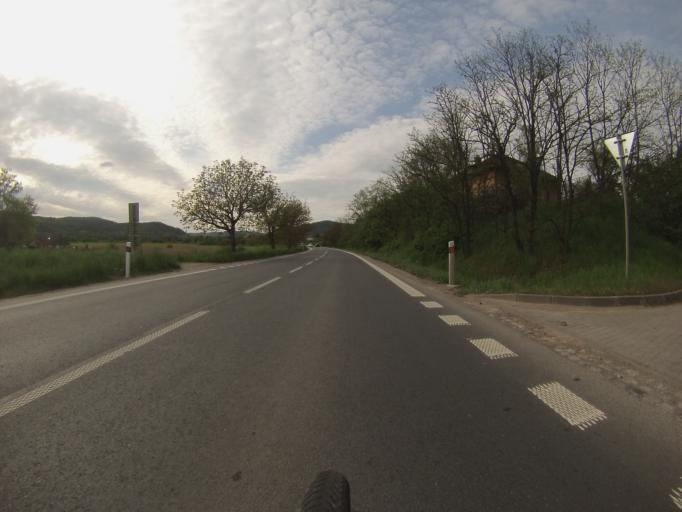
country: CZ
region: South Moravian
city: Tisnov
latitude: 49.3333
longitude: 16.4381
